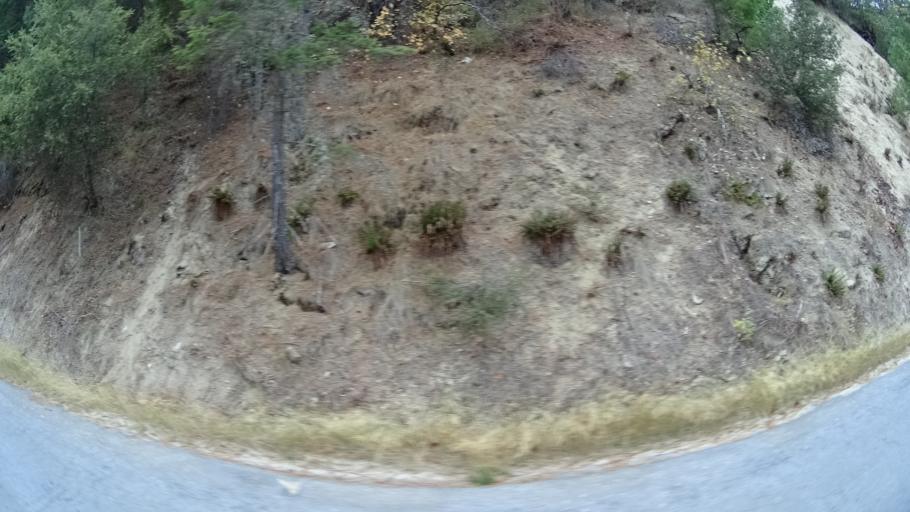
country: US
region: California
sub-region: Siskiyou County
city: Happy Camp
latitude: 41.8348
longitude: -123.1978
